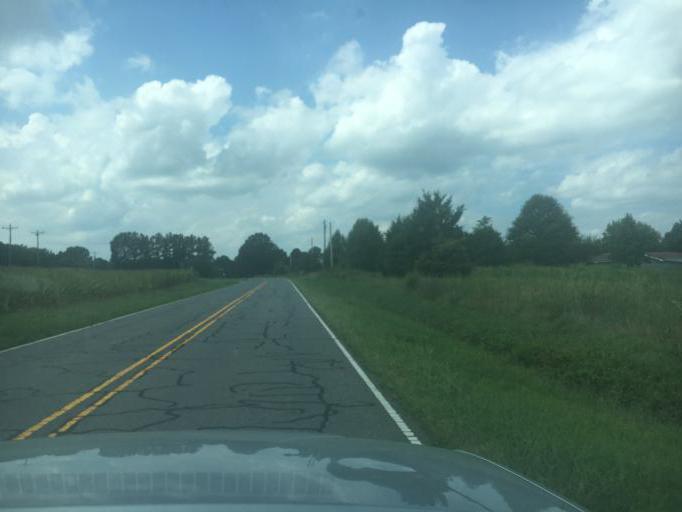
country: US
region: North Carolina
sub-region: Gaston County
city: Cherryville
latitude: 35.4531
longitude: -81.4304
